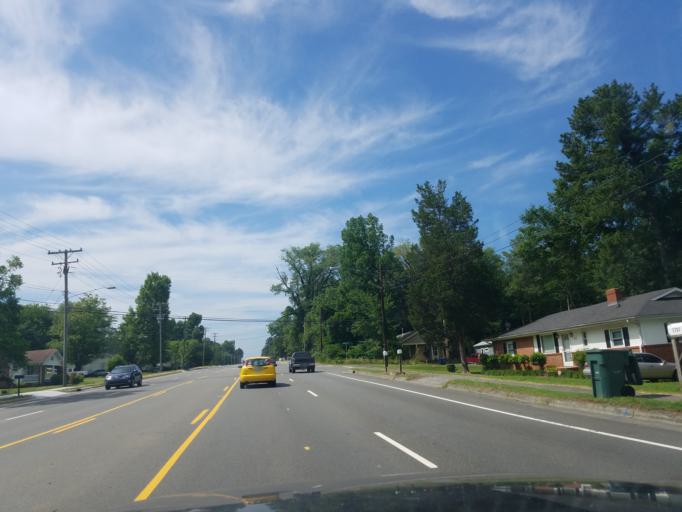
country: US
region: North Carolina
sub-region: Durham County
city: Durham
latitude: 36.0507
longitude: -78.9293
